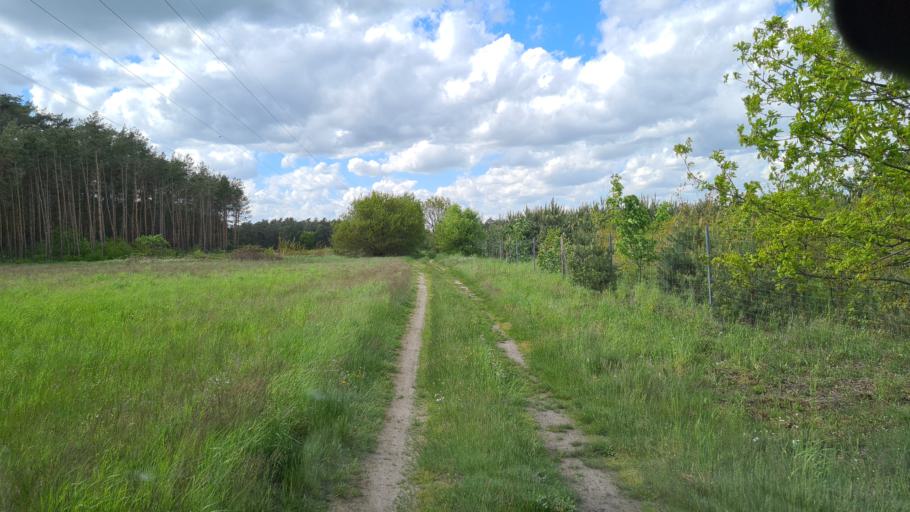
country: DE
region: Brandenburg
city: Crinitz
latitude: 51.7165
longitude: 13.7742
